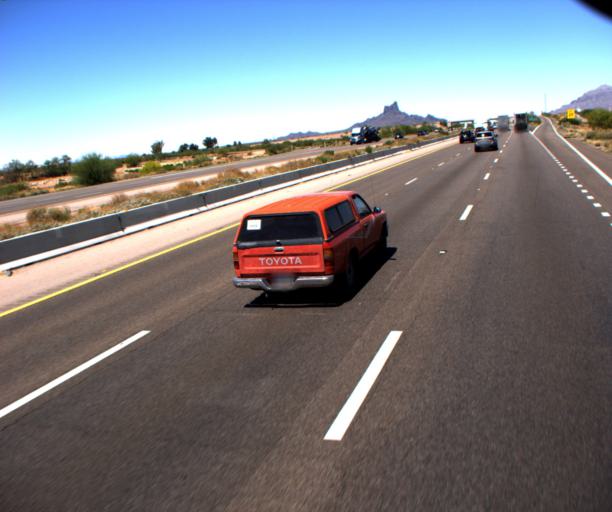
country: US
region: Arizona
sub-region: Pima County
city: Avra Valley
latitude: 32.5692
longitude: -111.3193
